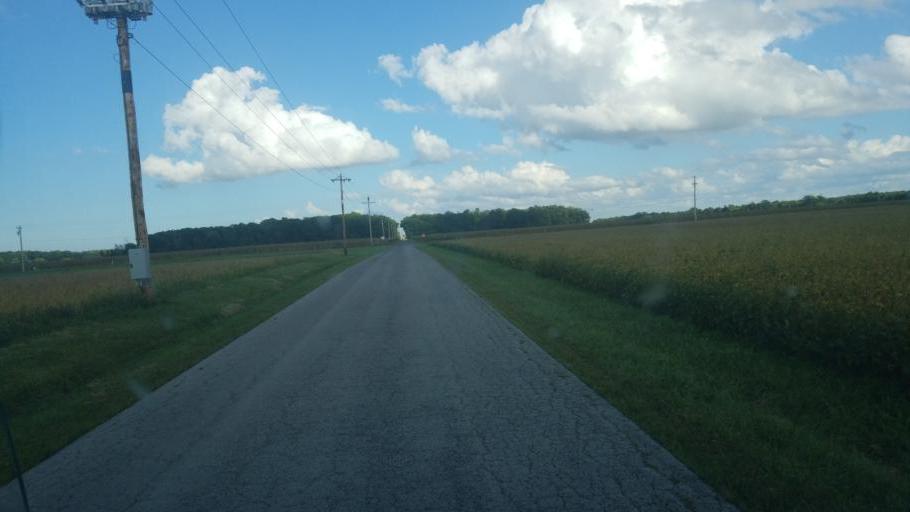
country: US
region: Ohio
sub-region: Hancock County
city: Arlington
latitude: 40.9363
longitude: -83.7294
